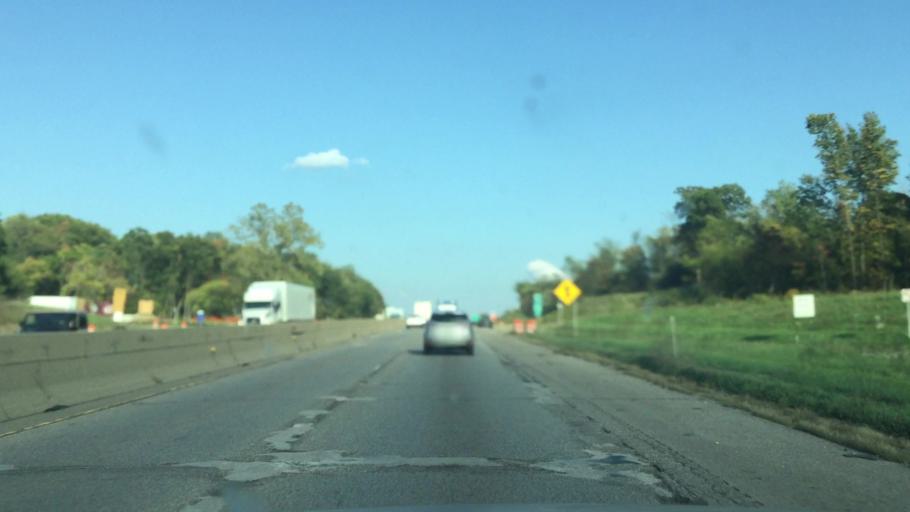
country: US
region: Michigan
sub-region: Jackson County
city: Jackson
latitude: 42.2721
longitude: -84.4016
